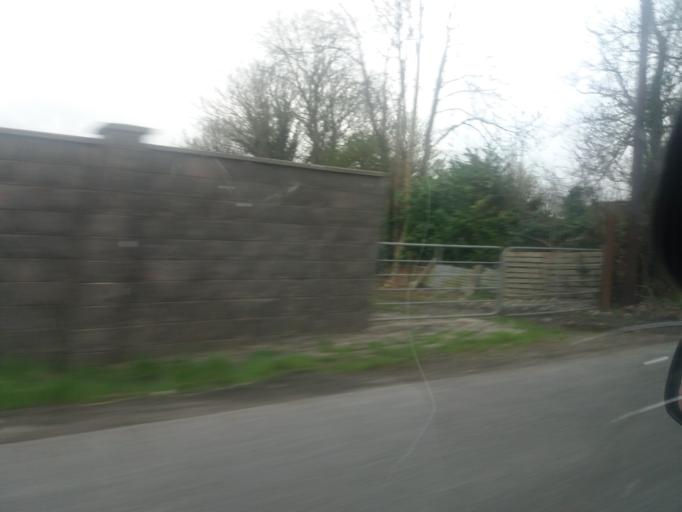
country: IE
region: Munster
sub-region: County Limerick
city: Newcastle West
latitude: 52.4819
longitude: -9.0104
